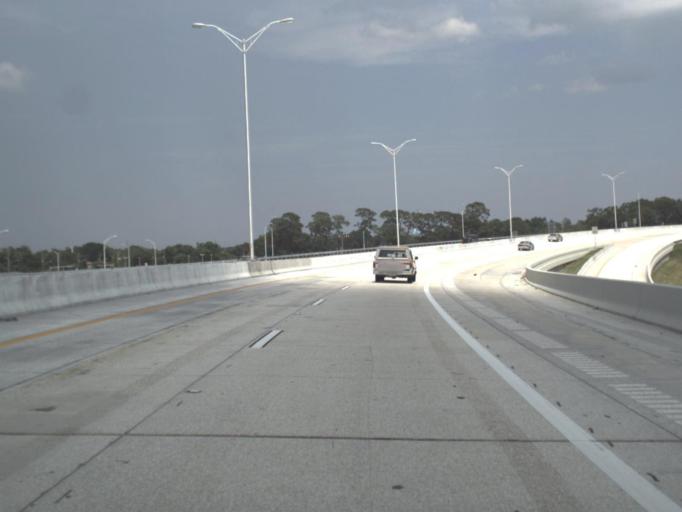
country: US
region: Florida
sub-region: Duval County
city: Jacksonville
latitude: 30.3562
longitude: -81.6407
